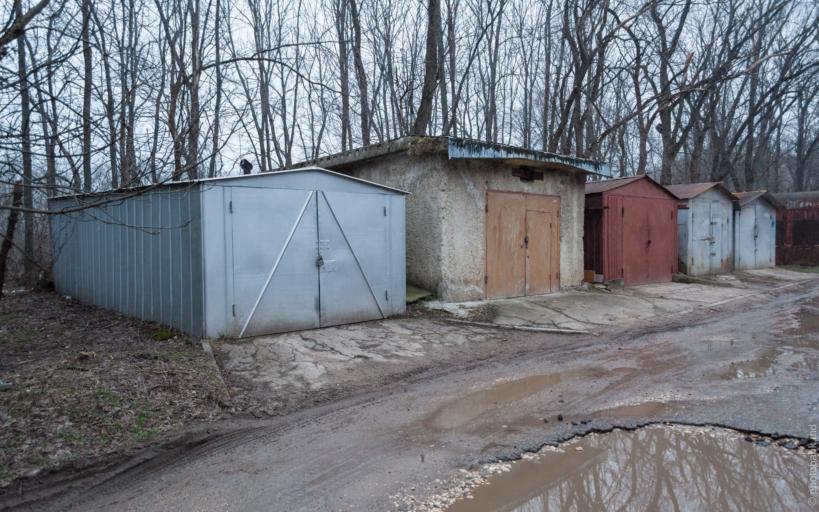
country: MD
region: Balti
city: Balti
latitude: 47.7898
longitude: 27.8989
